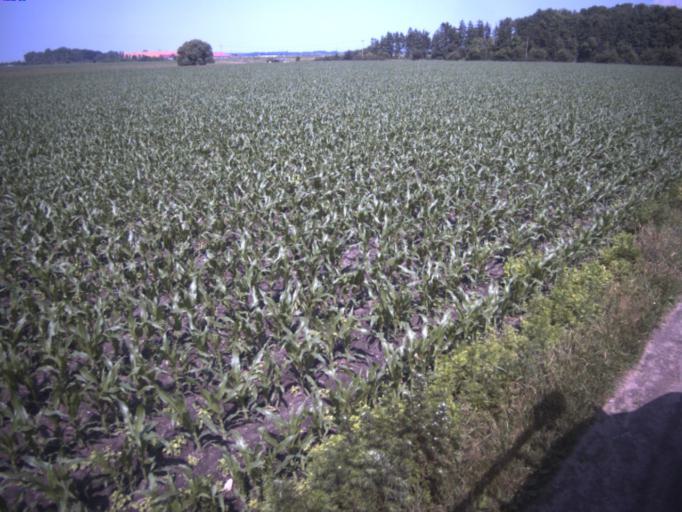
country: SE
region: Skane
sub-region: Angelholms Kommun
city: Strovelstorp
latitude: 56.1479
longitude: 12.7688
